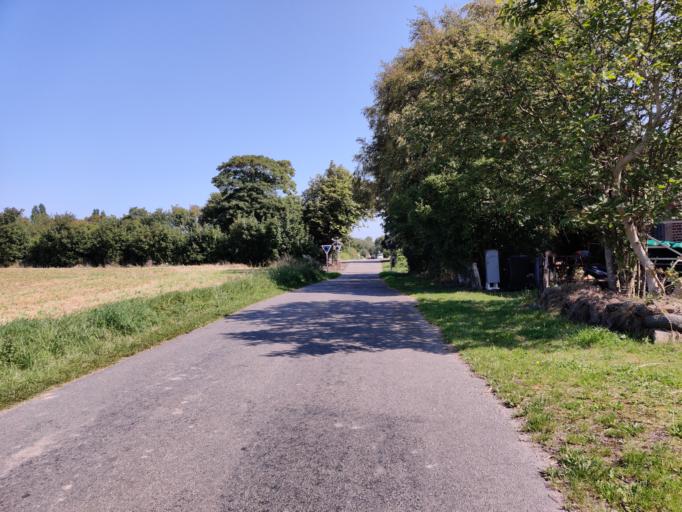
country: DK
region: Zealand
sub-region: Guldborgsund Kommune
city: Nykobing Falster
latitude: 54.6781
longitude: 11.8981
